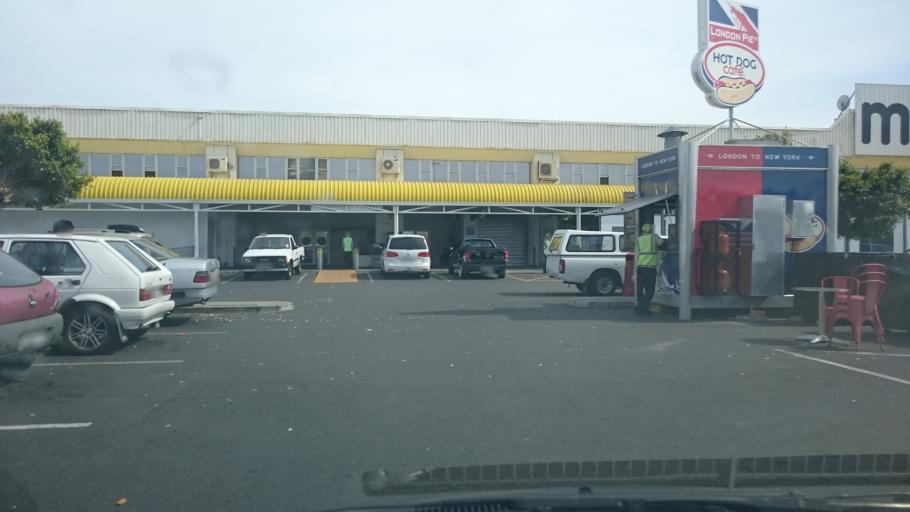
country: ZA
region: Western Cape
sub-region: City of Cape Town
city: Lansdowne
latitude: -34.0210
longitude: 18.5212
